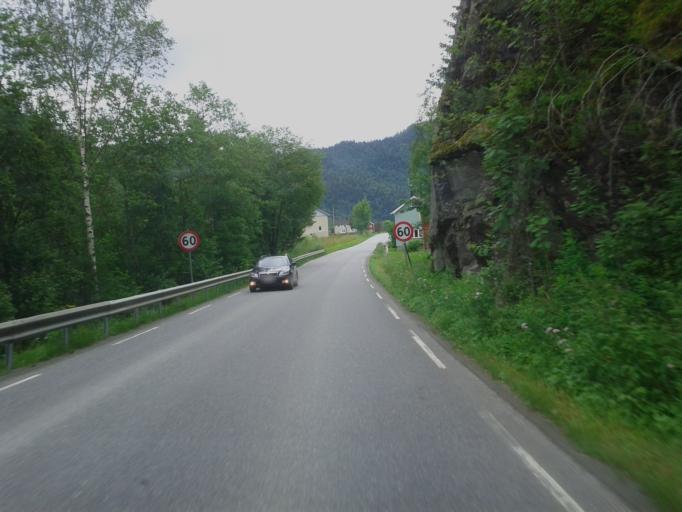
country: NO
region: Sor-Trondelag
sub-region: Midtre Gauldal
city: Storen
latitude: 63.0181
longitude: 10.4133
